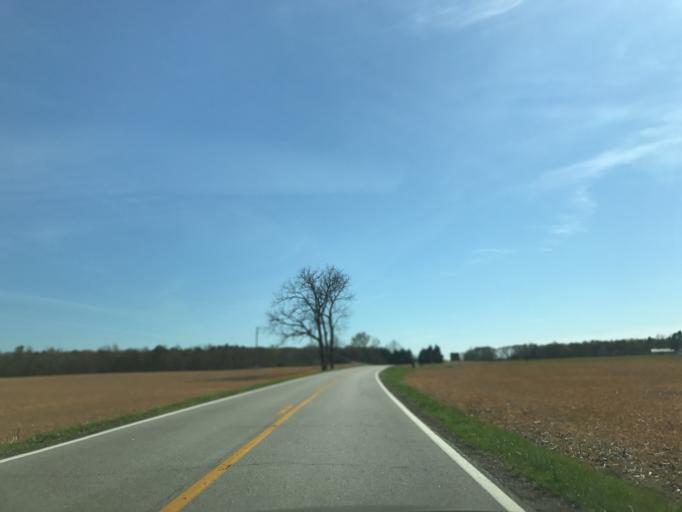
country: US
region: Maryland
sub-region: Caroline County
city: Ridgely
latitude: 38.9708
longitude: -75.9734
